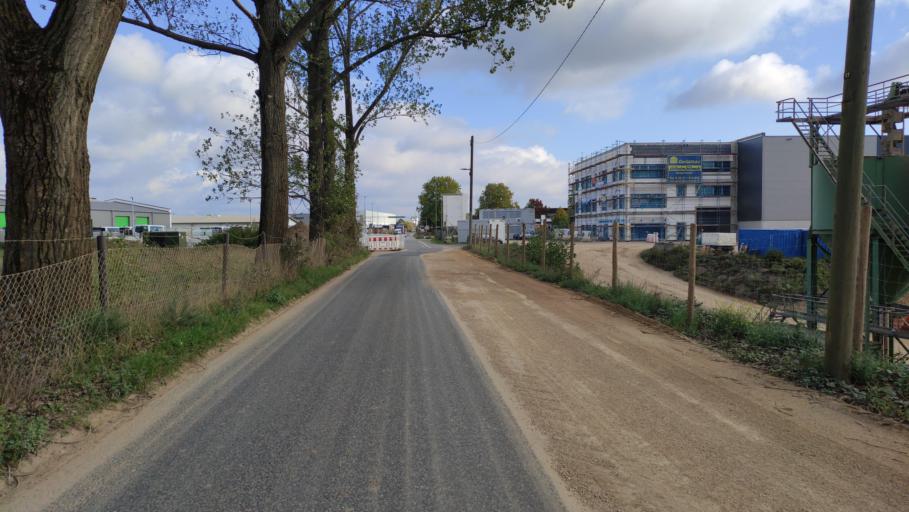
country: DE
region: North Rhine-Westphalia
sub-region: Regierungsbezirk Koln
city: Alfter
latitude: 50.7626
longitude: 7.0389
